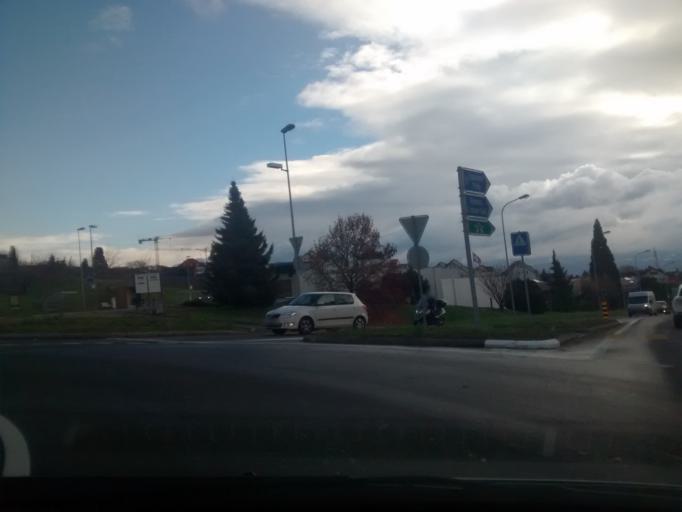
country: CH
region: Vaud
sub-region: Ouest Lausannois District
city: Crissier
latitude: 46.5560
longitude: 6.5729
